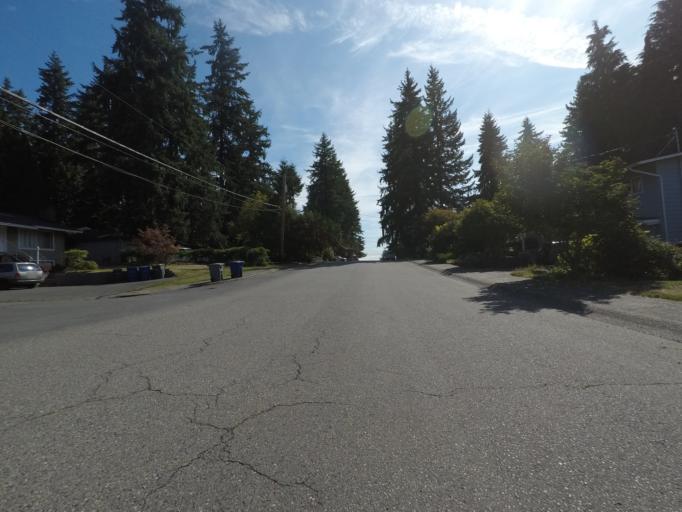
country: US
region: Washington
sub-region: King County
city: Inglewood-Finn Hill
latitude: 47.7333
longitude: -122.2315
